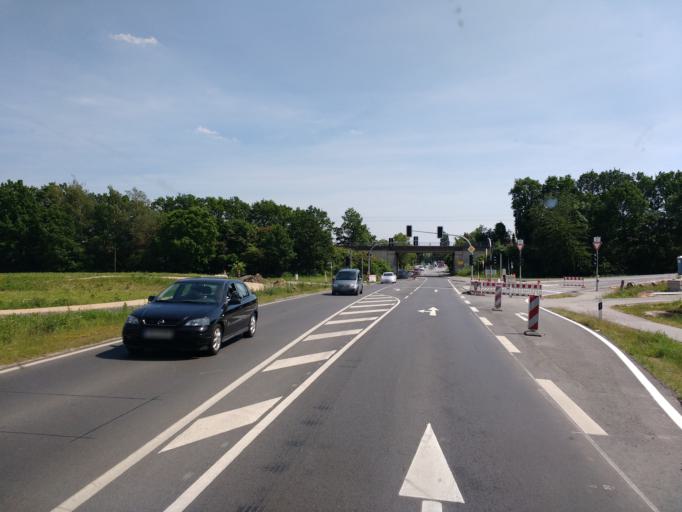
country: DE
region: Lower Saxony
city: Belm
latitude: 52.3076
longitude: 8.1203
